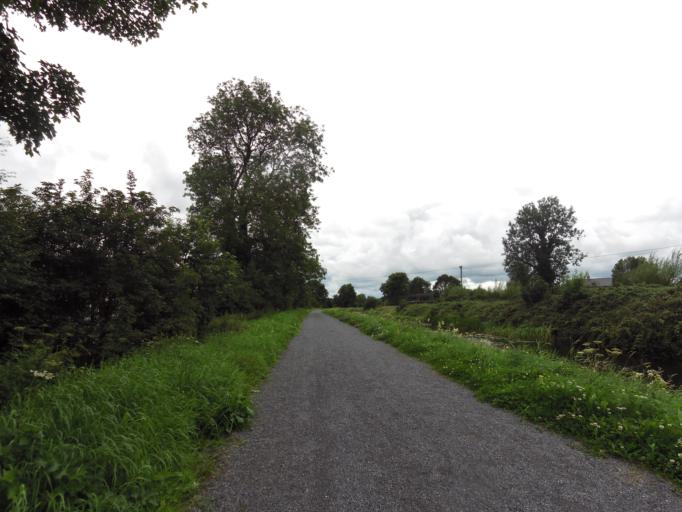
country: IE
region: Leinster
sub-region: An Iarmhi
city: An Muileann gCearr
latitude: 53.5081
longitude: -7.4177
